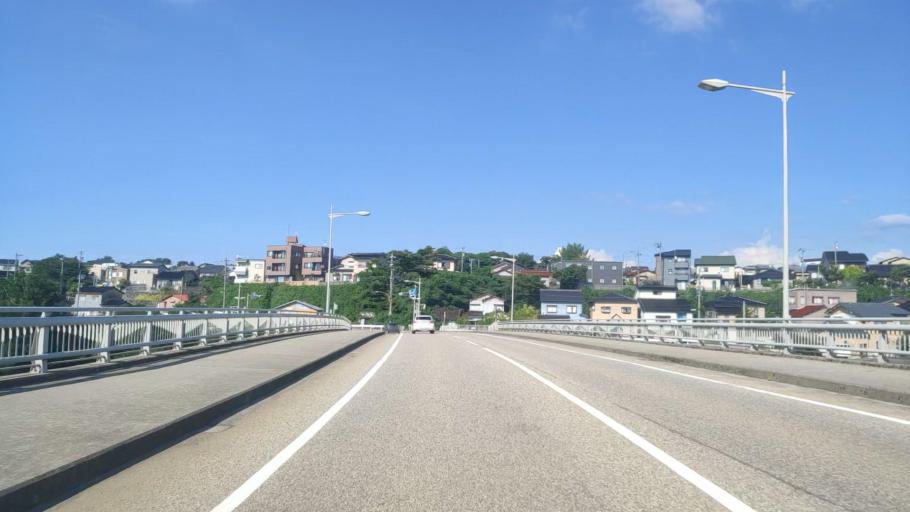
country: JP
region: Ishikawa
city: Nonoichi
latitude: 36.5384
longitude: 136.6779
